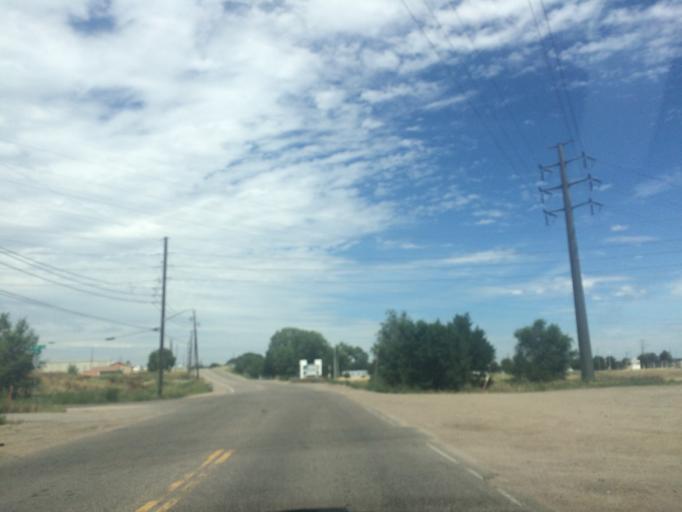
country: US
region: Colorado
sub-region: Adams County
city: Welby
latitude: 39.8122
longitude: -104.9594
